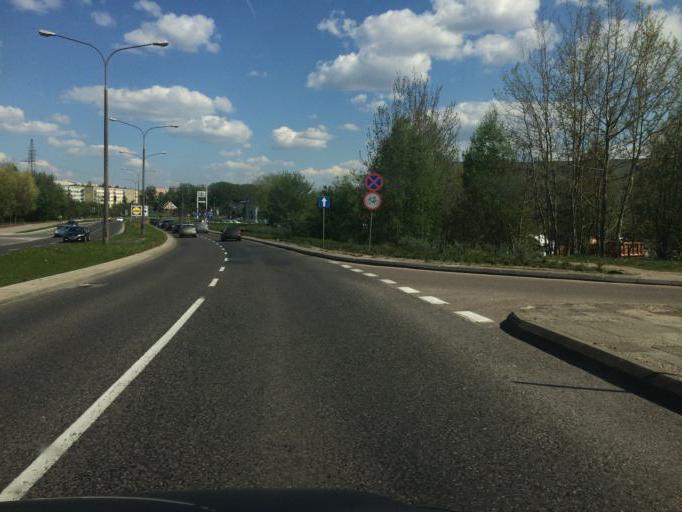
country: PL
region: Warmian-Masurian Voivodeship
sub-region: Olsztyn
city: Kortowo
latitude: 53.7658
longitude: 20.4683
